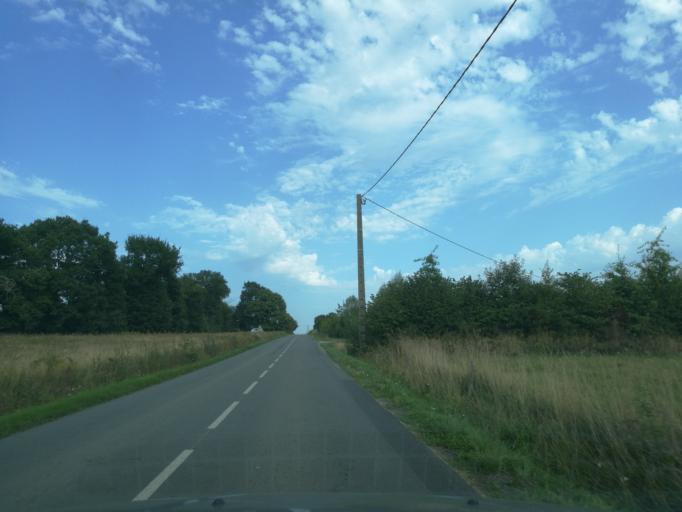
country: FR
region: Brittany
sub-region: Departement d'Ille-et-Vilaine
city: Montauban-de-Bretagne
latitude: 48.1995
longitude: -2.0181
